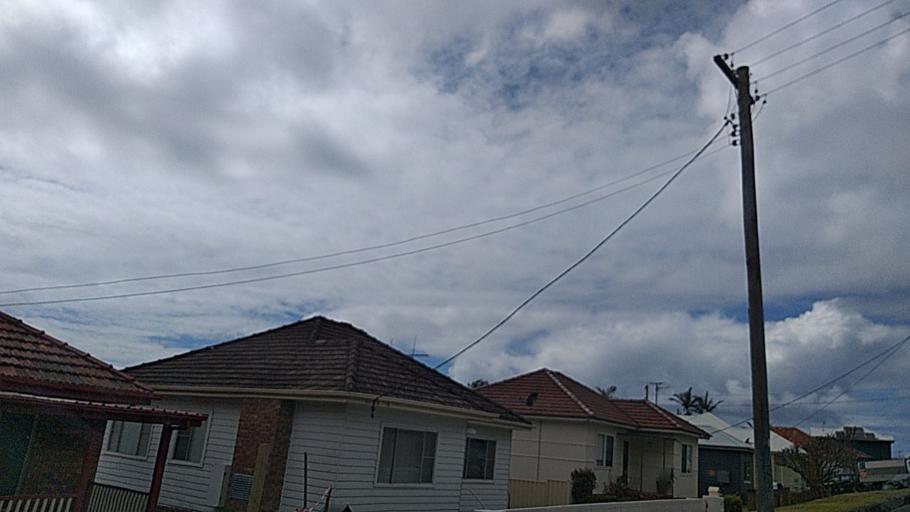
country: AU
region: New South Wales
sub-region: Wollongong
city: Bulli
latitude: -34.3243
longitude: 150.9143
